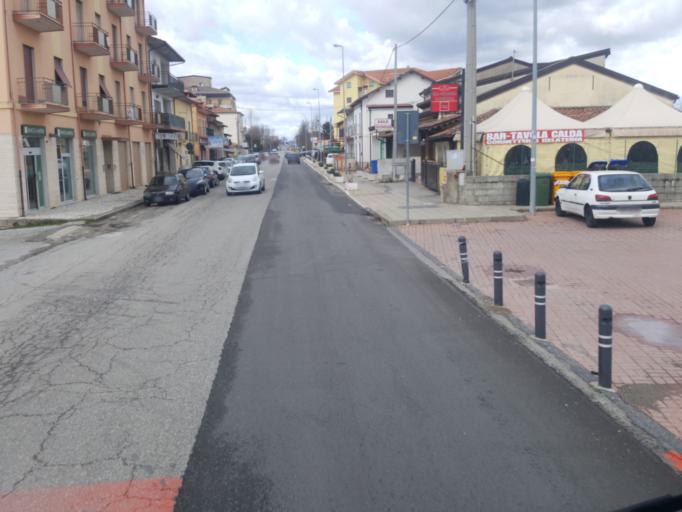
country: IT
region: Calabria
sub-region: Provincia di Cosenza
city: Santo Stefano di Rogliano
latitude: 39.2022
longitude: 16.3127
